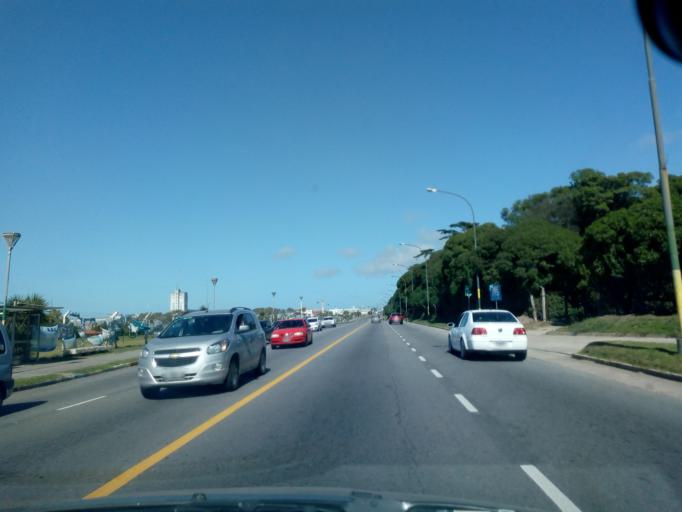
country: AR
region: Buenos Aires
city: Mar del Plata
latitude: -38.0364
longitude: -57.5388
